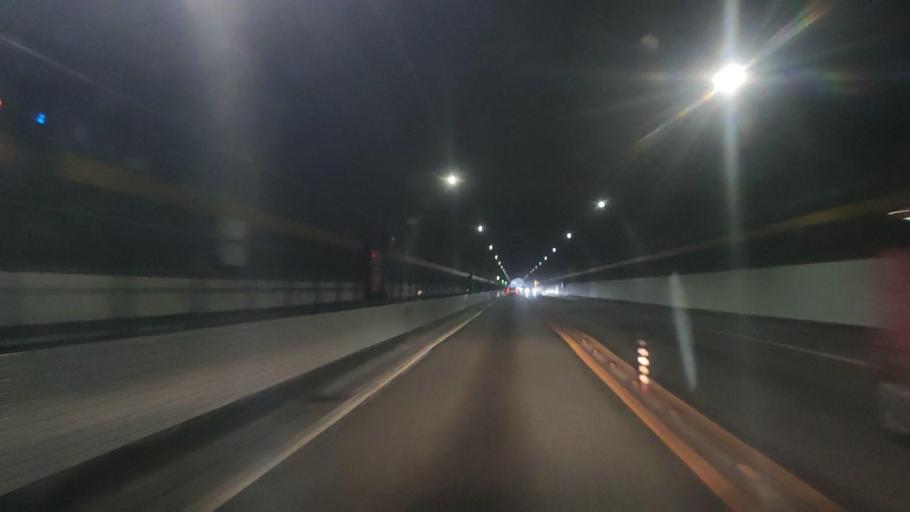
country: JP
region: Nagasaki
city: Nagasaki-shi
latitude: 32.7757
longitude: 129.8882
